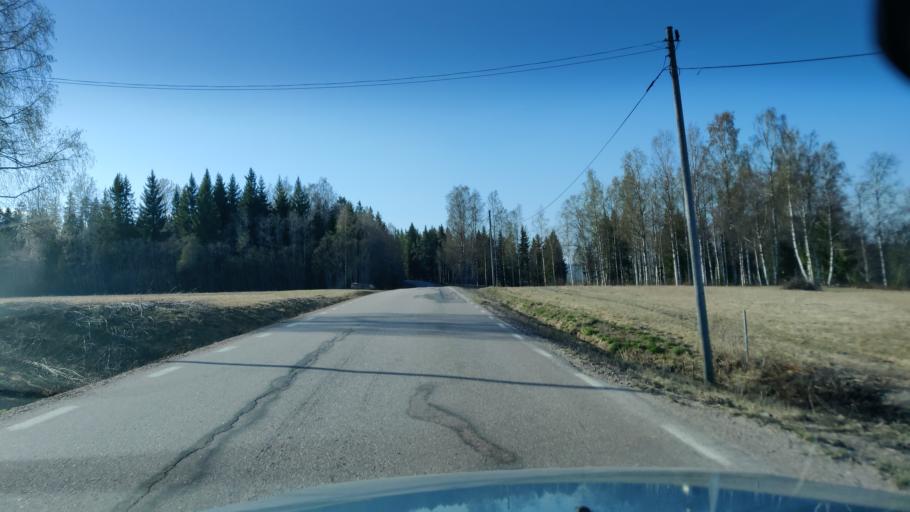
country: SE
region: Vaermland
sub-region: Munkfors Kommun
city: Munkfors
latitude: 59.9675
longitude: 13.4666
